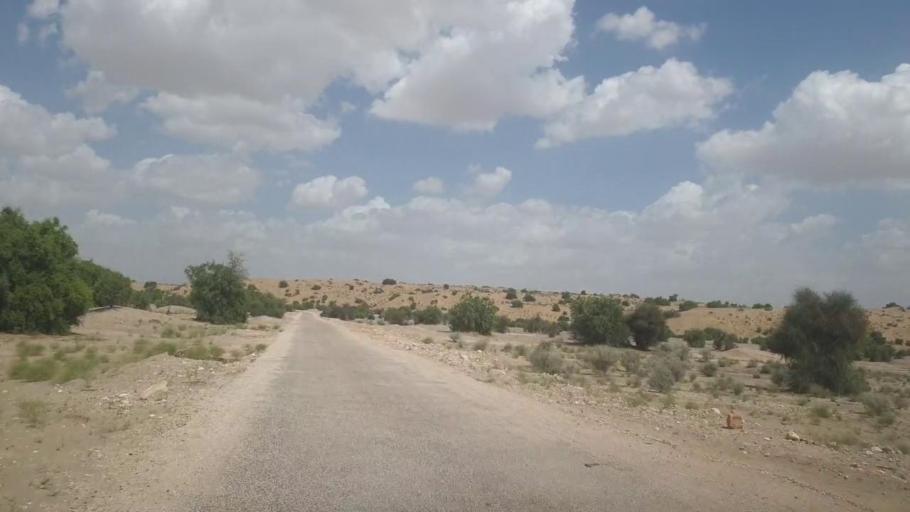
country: PK
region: Sindh
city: Kot Diji
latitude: 27.2528
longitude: 69.1578
